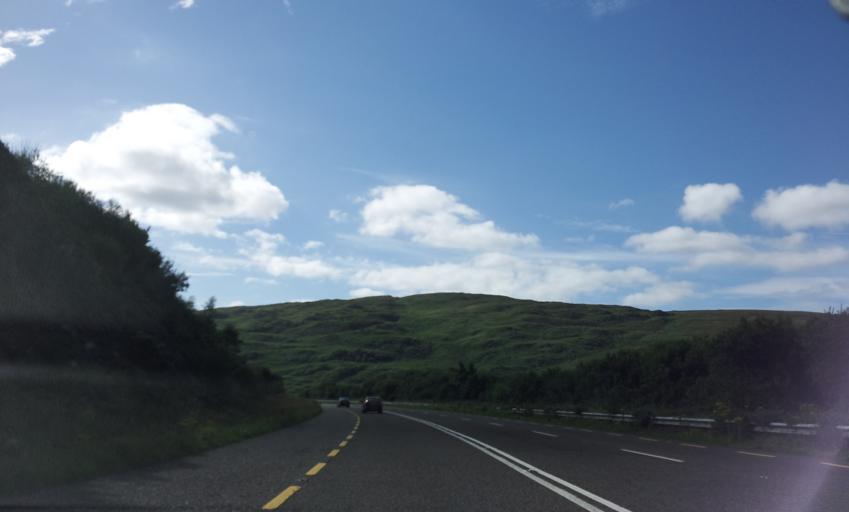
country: IE
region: Munster
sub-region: County Cork
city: Millstreet
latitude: 51.9872
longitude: -9.2868
